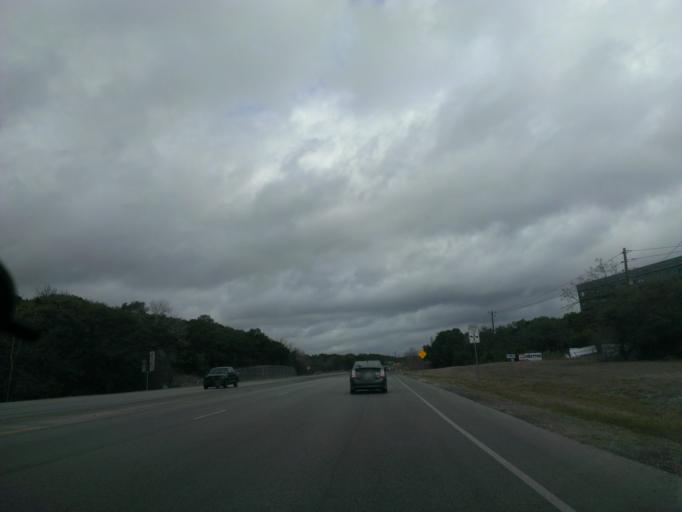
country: US
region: Texas
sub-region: Travis County
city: West Lake Hills
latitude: 30.3605
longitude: -97.7933
